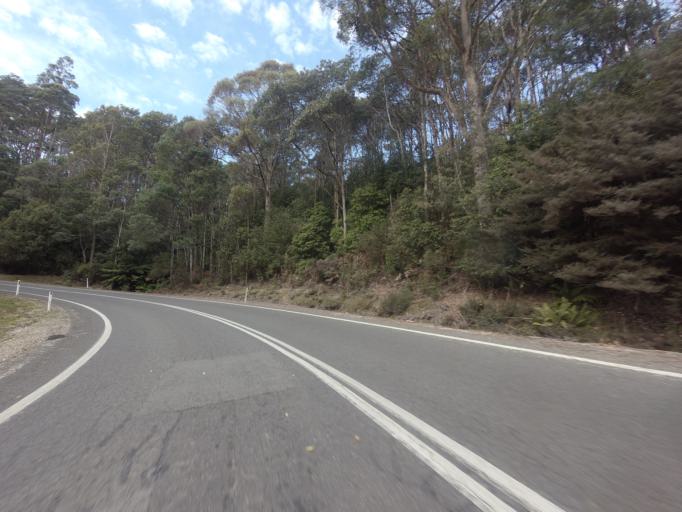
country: AU
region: Tasmania
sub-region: Meander Valley
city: Deloraine
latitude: -41.6546
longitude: 146.7161
